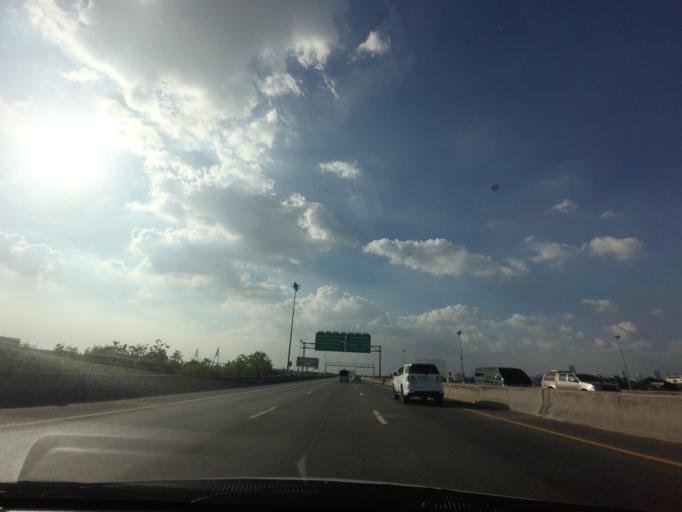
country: TH
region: Samut Prakan
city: Phra Samut Chedi
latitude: 13.6354
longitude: 100.5654
